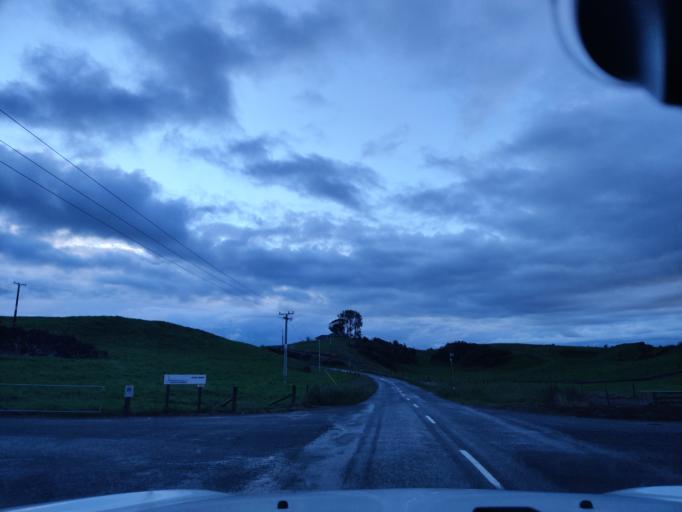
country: NZ
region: Waikato
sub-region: South Waikato District
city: Tokoroa
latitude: -38.1805
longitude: 175.7818
